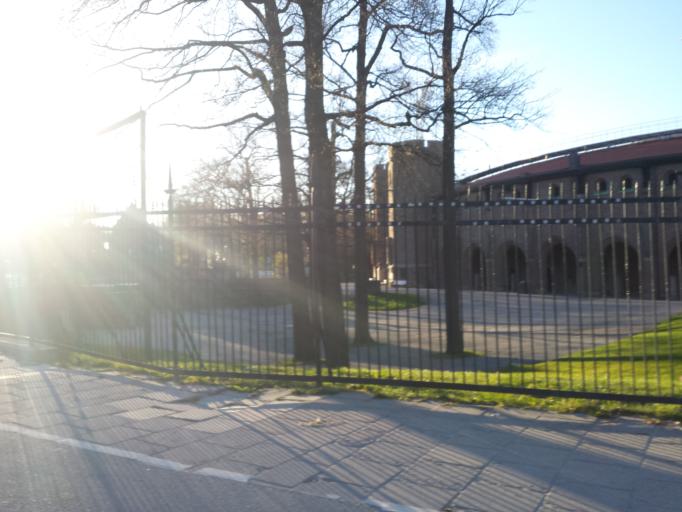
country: SE
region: Stockholm
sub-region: Stockholms Kommun
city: OEstermalm
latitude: 59.3440
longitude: 18.0790
